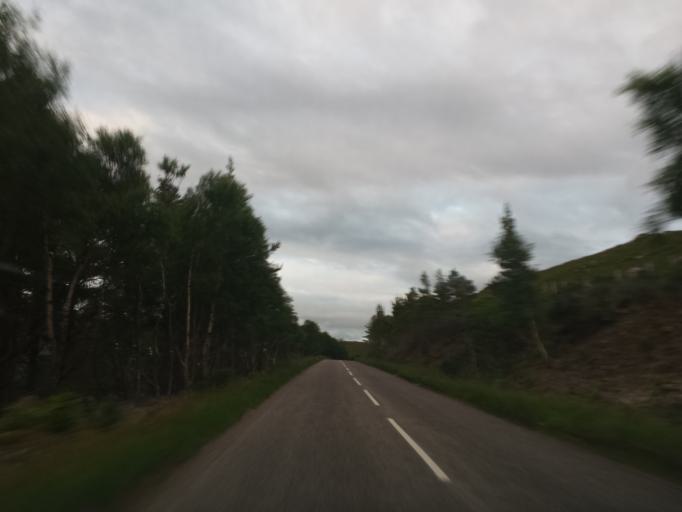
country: GB
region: Scotland
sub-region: Highland
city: Ullapool
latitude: 57.5270
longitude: -5.5795
